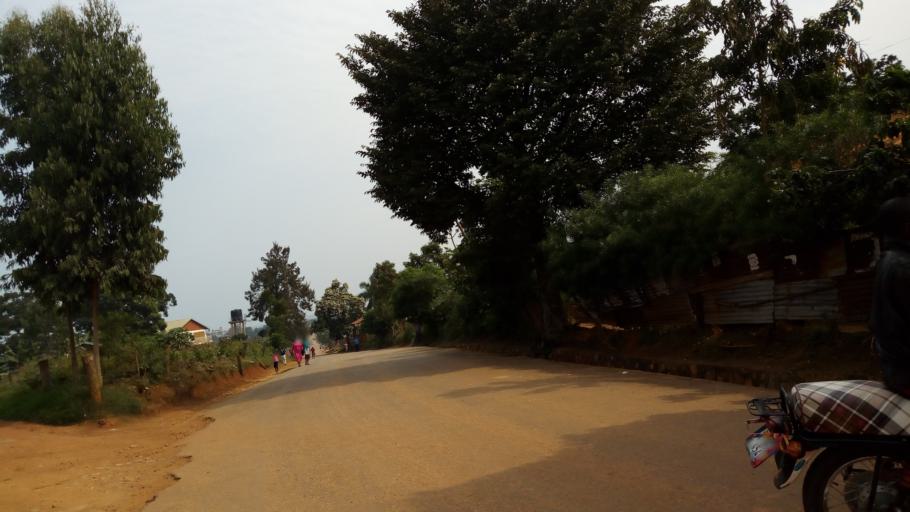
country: UG
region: Central Region
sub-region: Wakiso District
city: Kireka
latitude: 0.3097
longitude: 32.6536
